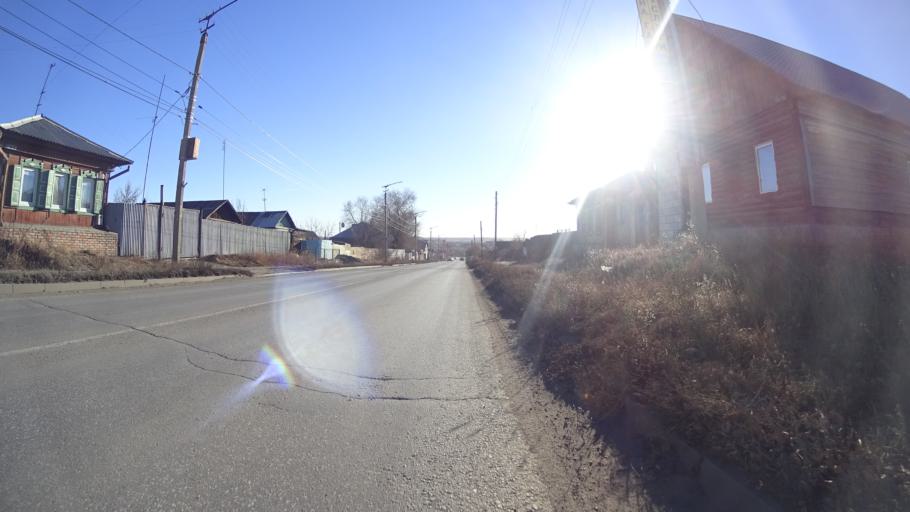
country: RU
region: Chelyabinsk
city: Troitsk
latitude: 54.1000
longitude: 61.5625
